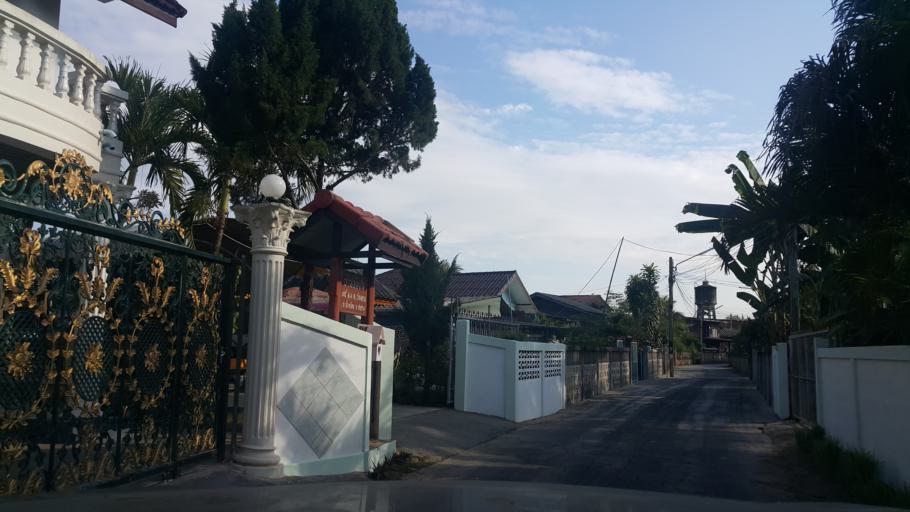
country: TH
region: Lampang
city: Hang Chat
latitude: 18.3125
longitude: 99.3530
